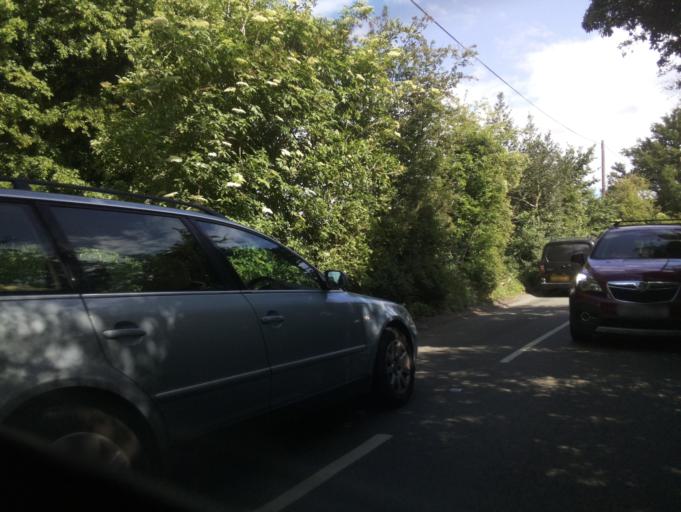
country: GB
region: England
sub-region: Hertfordshire
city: Chorleywood
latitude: 51.6636
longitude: -0.4636
